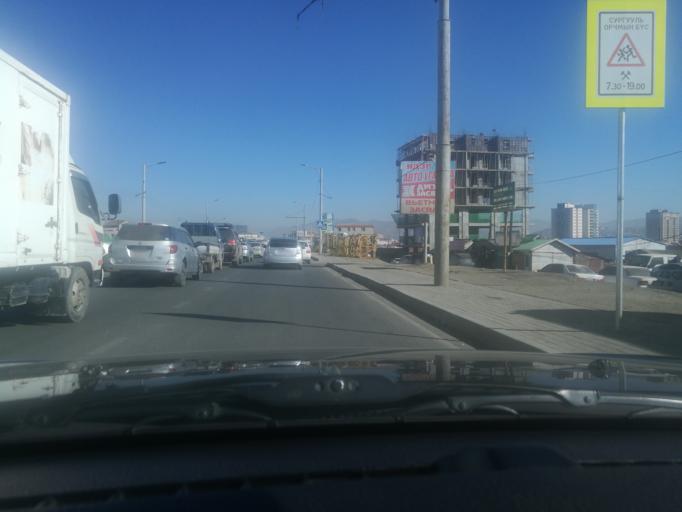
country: MN
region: Ulaanbaatar
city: Ulaanbaatar
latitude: 47.9346
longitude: 106.9073
